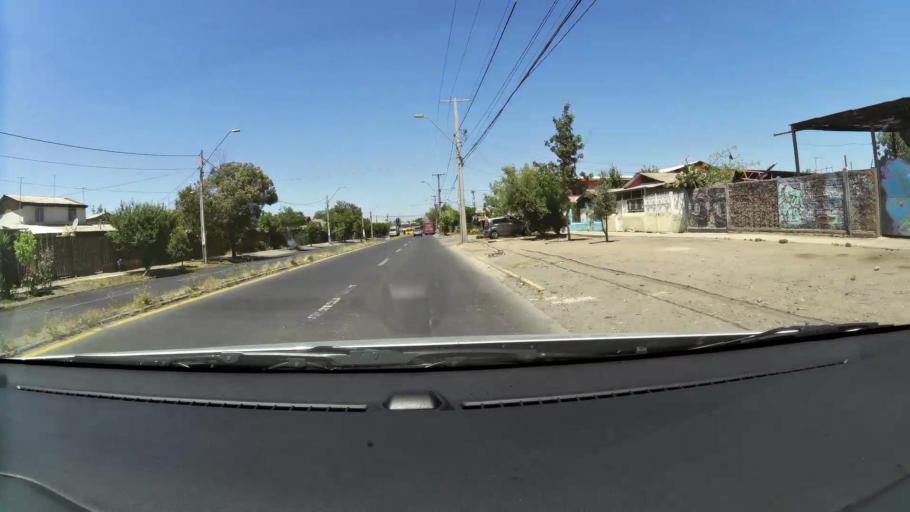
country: CL
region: Santiago Metropolitan
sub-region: Provincia de Santiago
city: La Pintana
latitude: -33.5722
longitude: -70.6596
